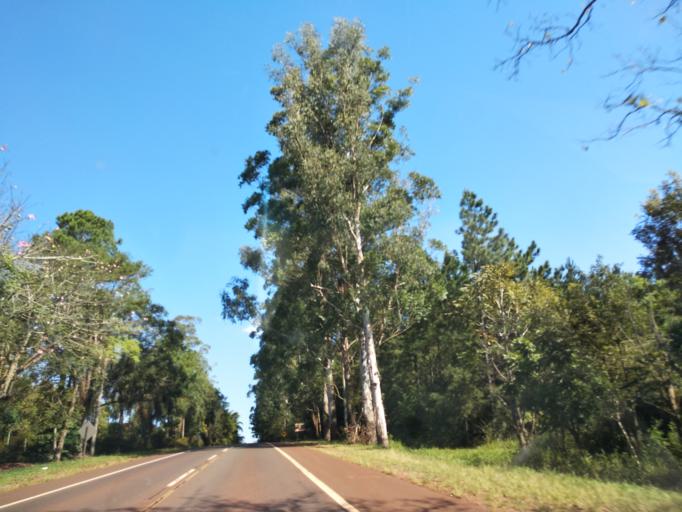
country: AR
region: Misiones
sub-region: Departamento de Montecarlo
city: Montecarlo
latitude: -26.5602
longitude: -54.7246
